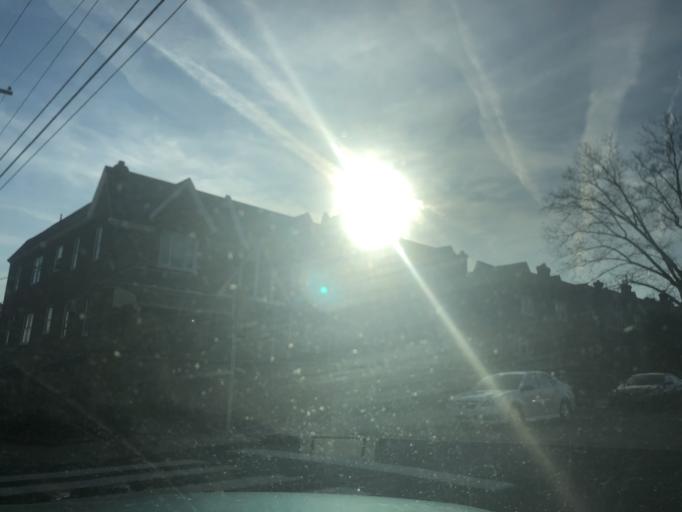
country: US
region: Pennsylvania
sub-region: Delaware County
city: Millbourne
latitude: 39.9795
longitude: -75.2359
